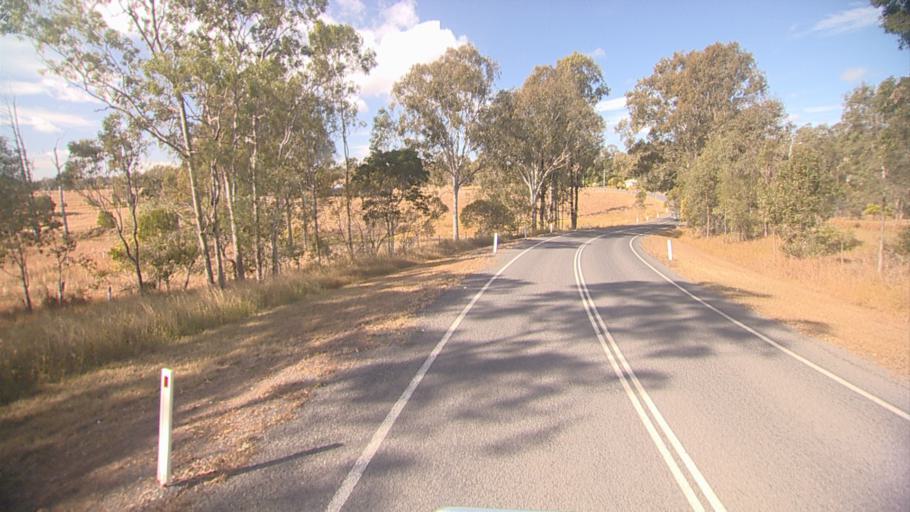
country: AU
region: Queensland
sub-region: Logan
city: Cedar Vale
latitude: -27.8652
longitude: 153.0080
